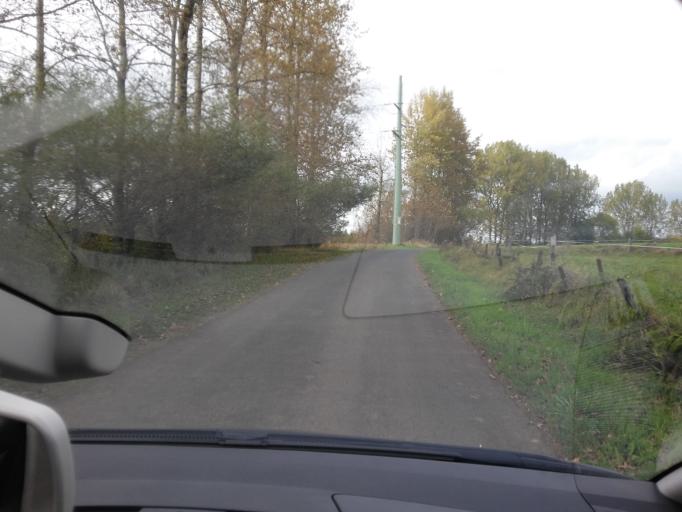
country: BE
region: Wallonia
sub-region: Province du Luxembourg
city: Arlon
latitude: 49.7013
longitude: 5.7907
